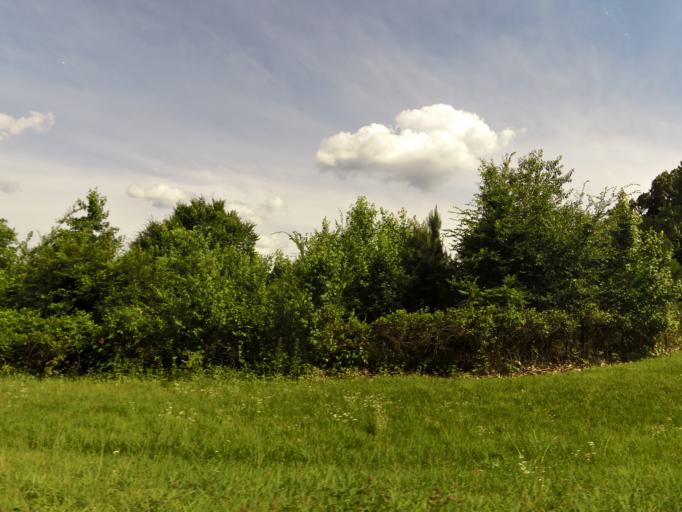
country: US
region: Tennessee
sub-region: Carroll County
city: Bruceton
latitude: 36.0362
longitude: -88.3185
